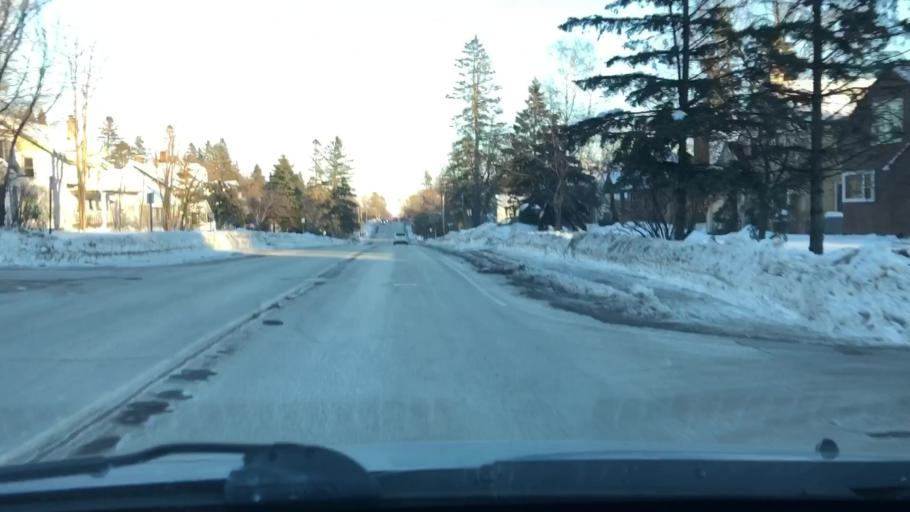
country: US
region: Minnesota
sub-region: Saint Louis County
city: Duluth
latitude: 46.8257
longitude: -92.0769
